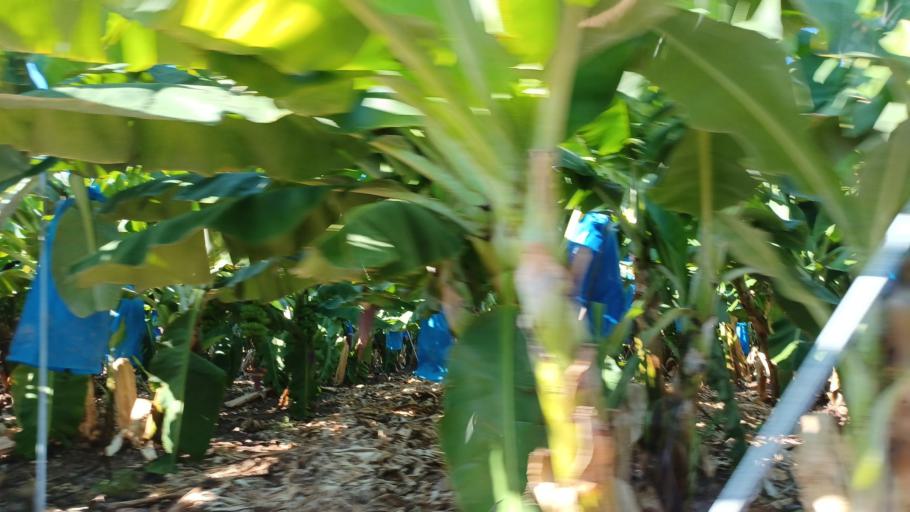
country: CY
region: Pafos
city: Kissonerga
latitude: 34.8481
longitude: 32.3873
